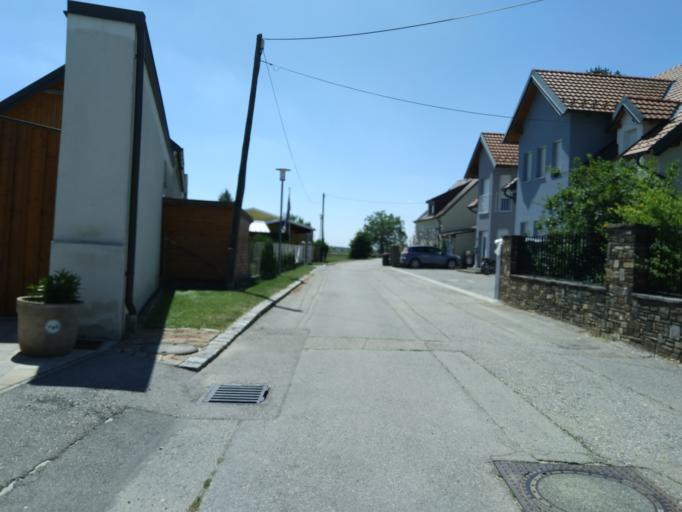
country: AT
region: Lower Austria
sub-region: Politischer Bezirk Mistelbach
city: Bockfliess
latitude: 48.3583
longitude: 16.5945
